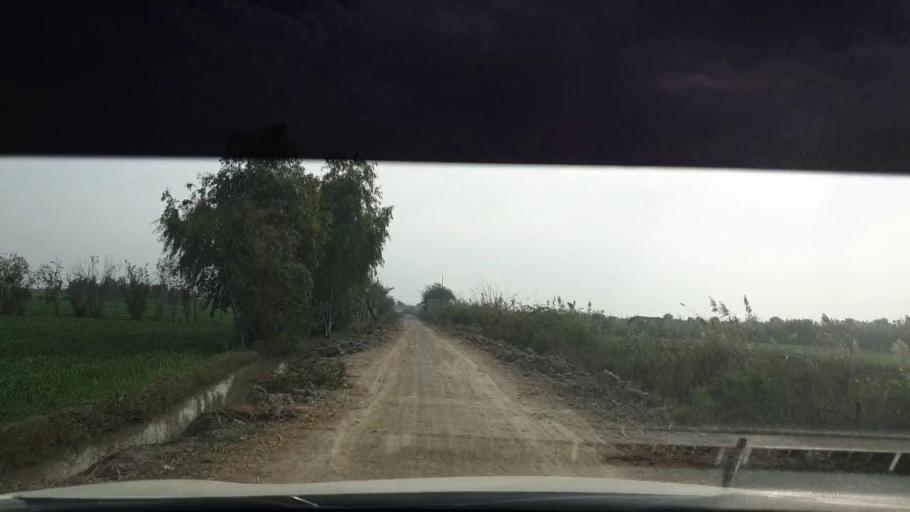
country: PK
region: Sindh
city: Berani
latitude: 25.7510
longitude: 68.8770
